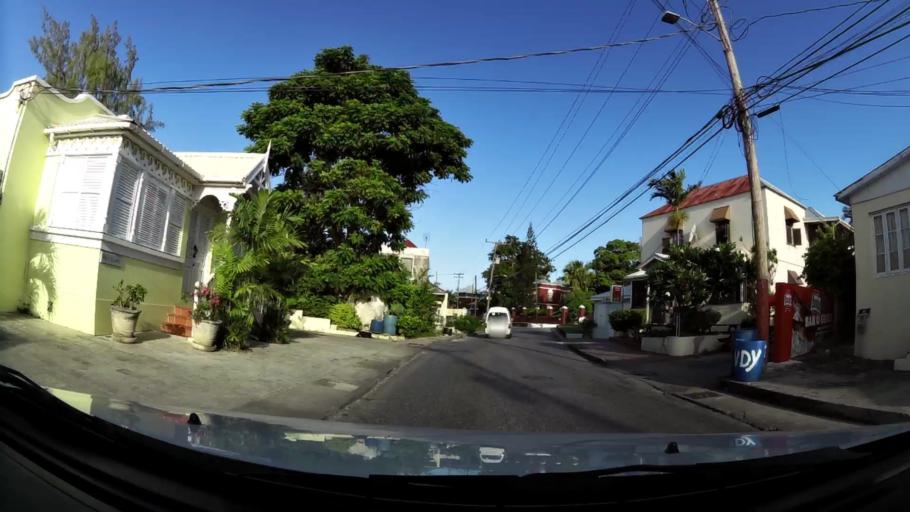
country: BB
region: Saint Michael
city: Bridgetown
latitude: 13.0752
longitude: -59.6002
